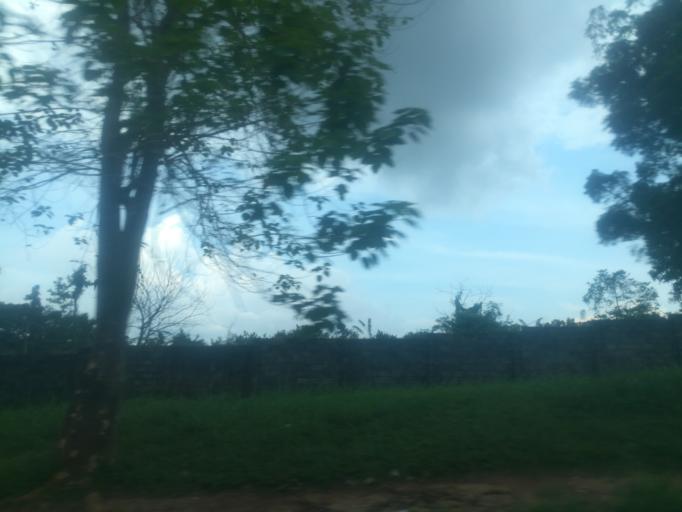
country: NG
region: Oyo
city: Ibadan
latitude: 7.4355
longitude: 3.8867
